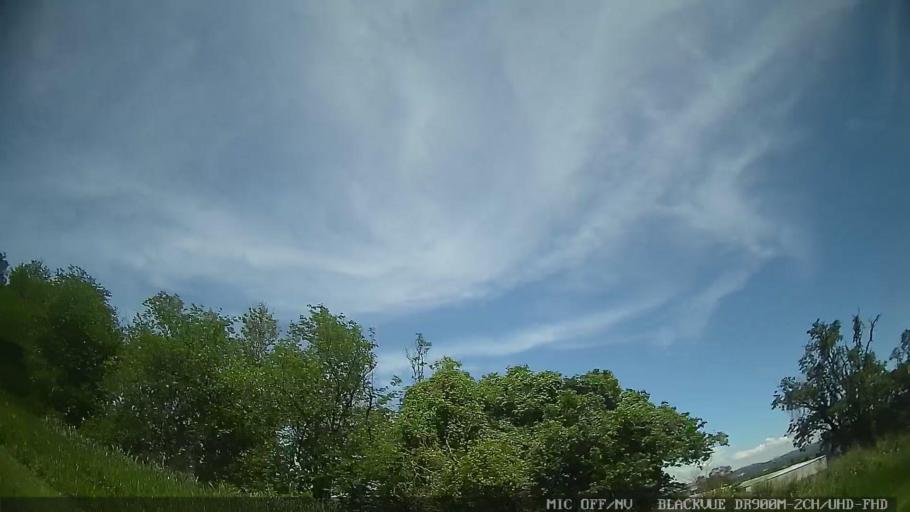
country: BR
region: Sao Paulo
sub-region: Jaguariuna
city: Jaguariuna
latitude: -22.6550
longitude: -47.0042
